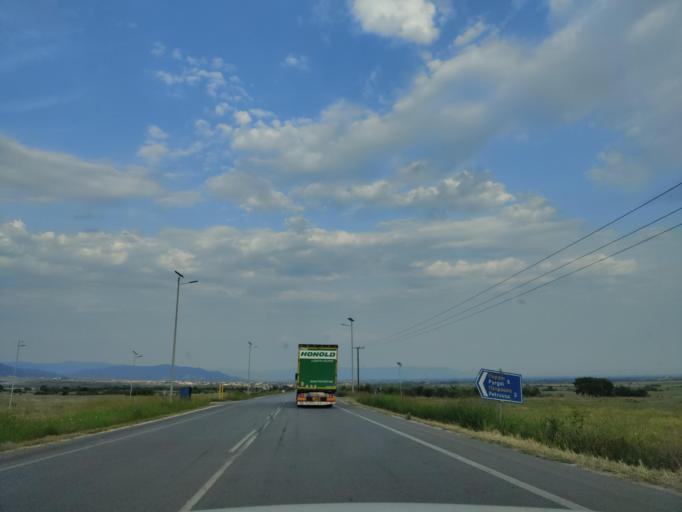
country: GR
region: East Macedonia and Thrace
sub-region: Nomos Dramas
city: Petroussa
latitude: 41.1740
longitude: 24.0196
